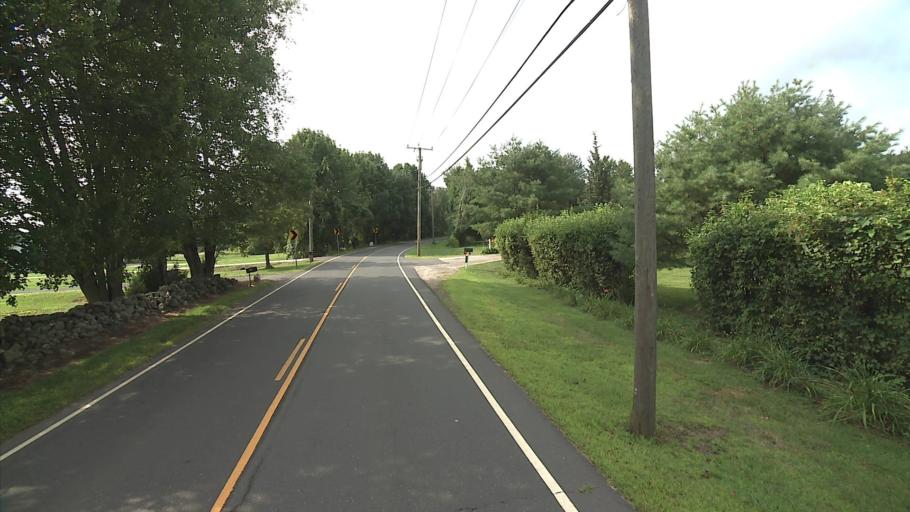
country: US
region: Connecticut
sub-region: Middlesex County
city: Moodus
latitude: 41.5373
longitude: -72.4108
